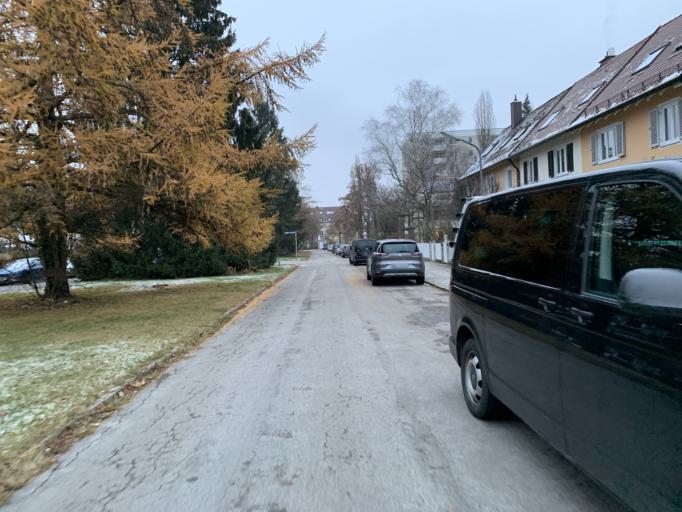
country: DE
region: Bavaria
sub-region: Upper Bavaria
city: Munich
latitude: 48.1035
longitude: 11.5757
